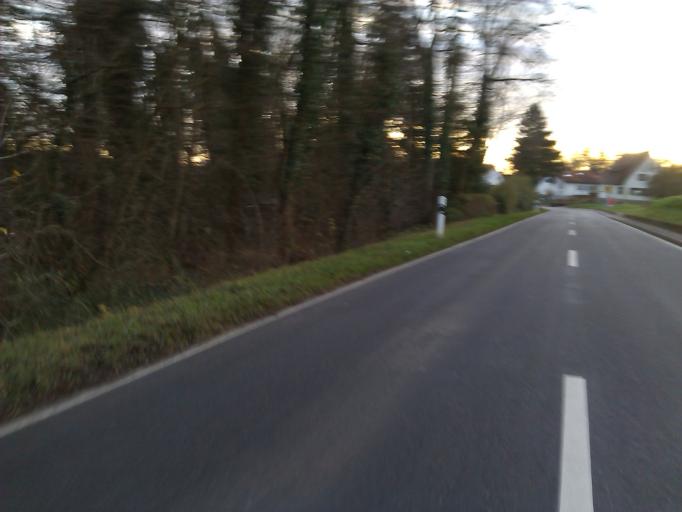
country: DE
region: Baden-Wuerttemberg
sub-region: Regierungsbezirk Stuttgart
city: Oedheim
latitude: 49.2453
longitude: 9.2282
